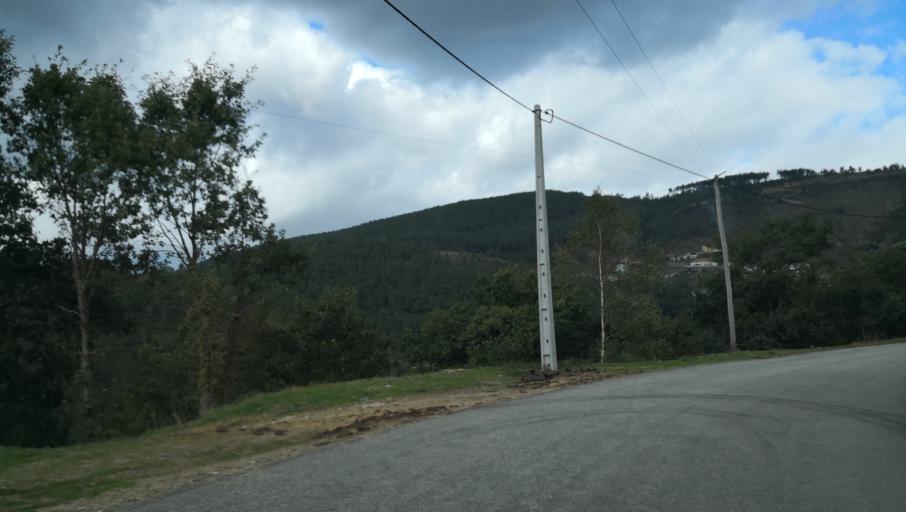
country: PT
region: Vila Real
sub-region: Vila Real
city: Vila Real
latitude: 41.3615
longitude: -7.8455
